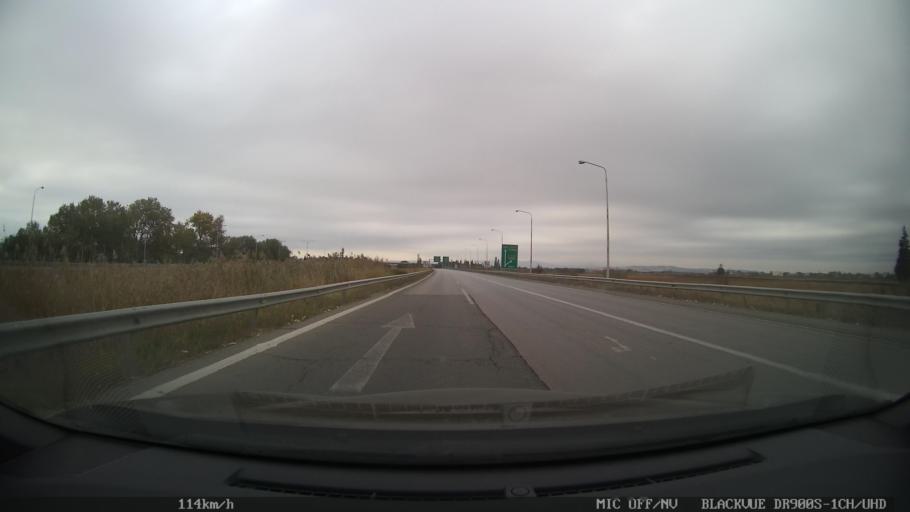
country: GR
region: Central Macedonia
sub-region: Nomos Imathias
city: Kleidi
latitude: 40.5613
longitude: 22.6043
